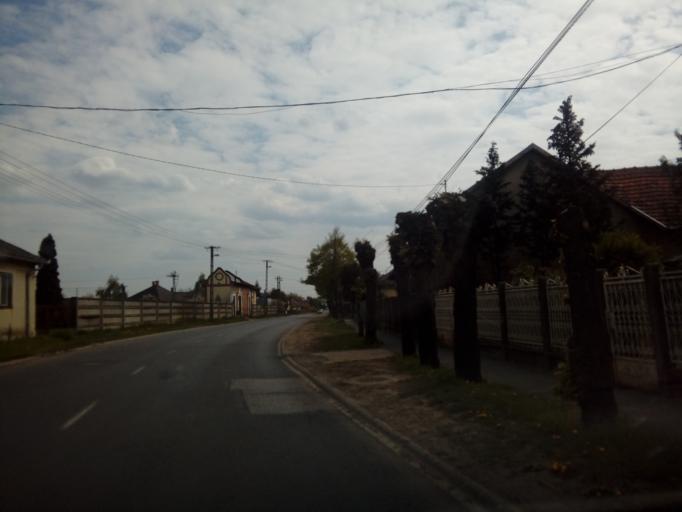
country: HU
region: Szabolcs-Szatmar-Bereg
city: Nagykallo
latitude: 47.8714
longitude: 21.8467
